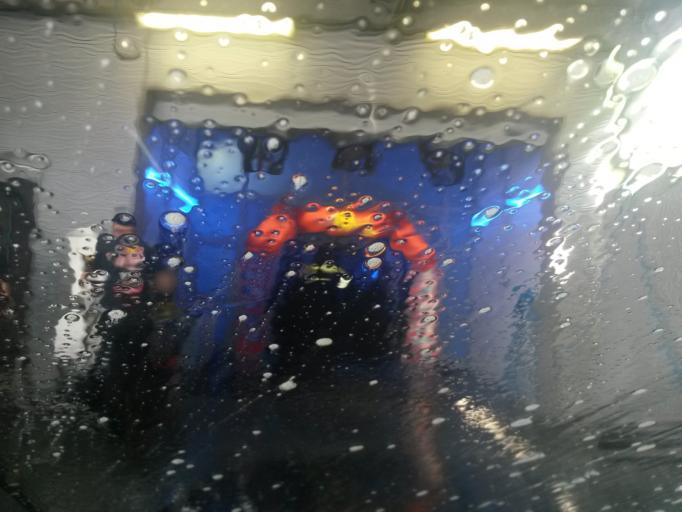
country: DE
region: Bavaria
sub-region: Regierungsbezirk Unterfranken
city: Gerbrunn
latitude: 49.7958
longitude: 9.9800
